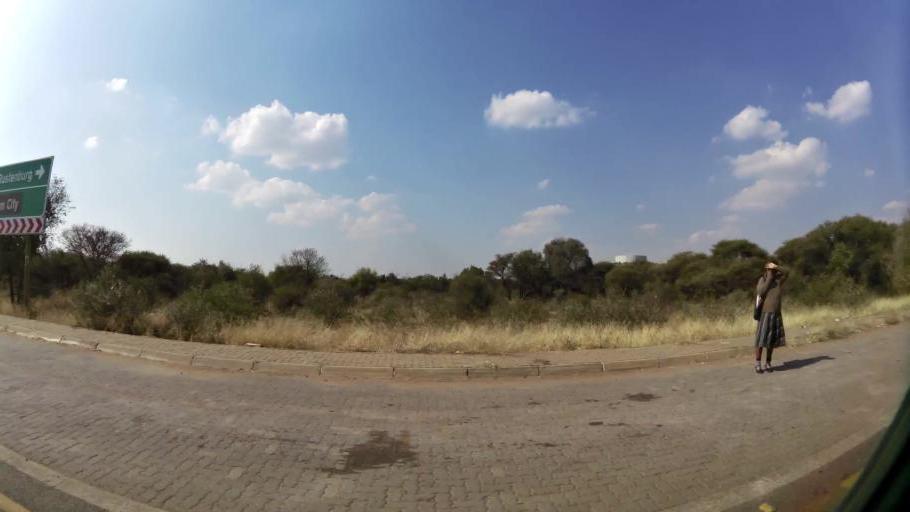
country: ZA
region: North-West
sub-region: Bojanala Platinum District Municipality
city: Mogwase
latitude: -25.4294
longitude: 27.0818
